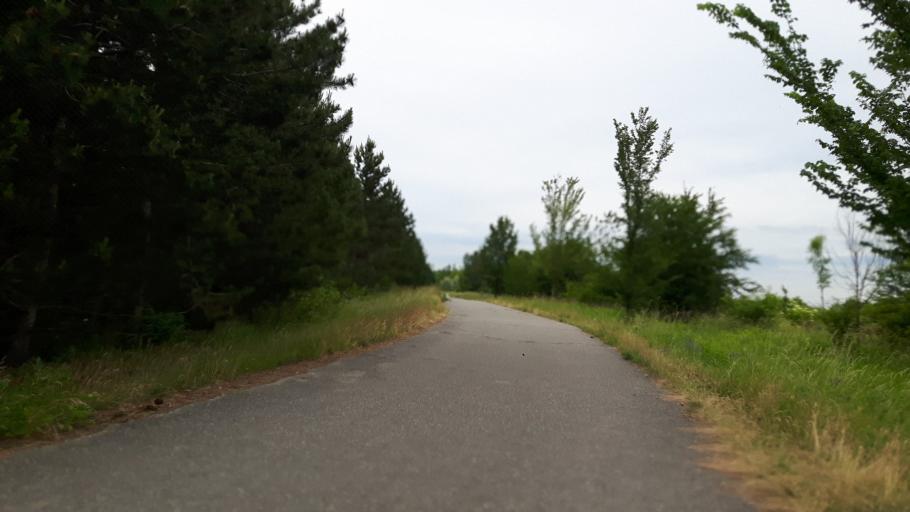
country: DE
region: Saxony
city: Zwochau
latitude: 51.4273
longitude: 12.3183
